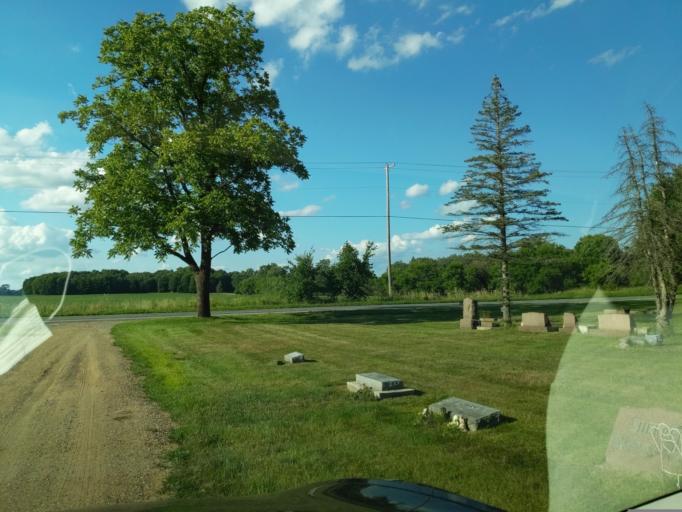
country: US
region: Michigan
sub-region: Ingham County
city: Holt
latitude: 42.5818
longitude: -84.5389
